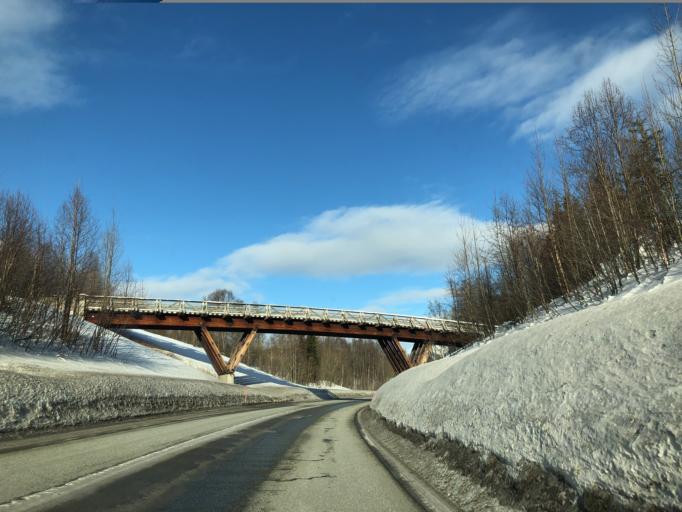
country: NO
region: Troms
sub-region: Malselv
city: Moen
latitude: 69.0702
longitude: 18.5309
